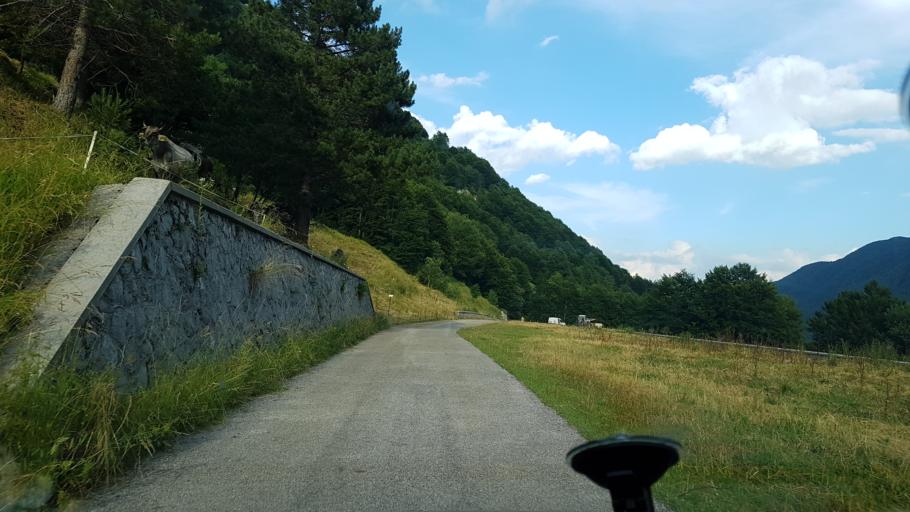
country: IT
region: Friuli Venezia Giulia
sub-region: Provincia di Udine
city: Prato
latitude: 46.3358
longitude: 13.3278
